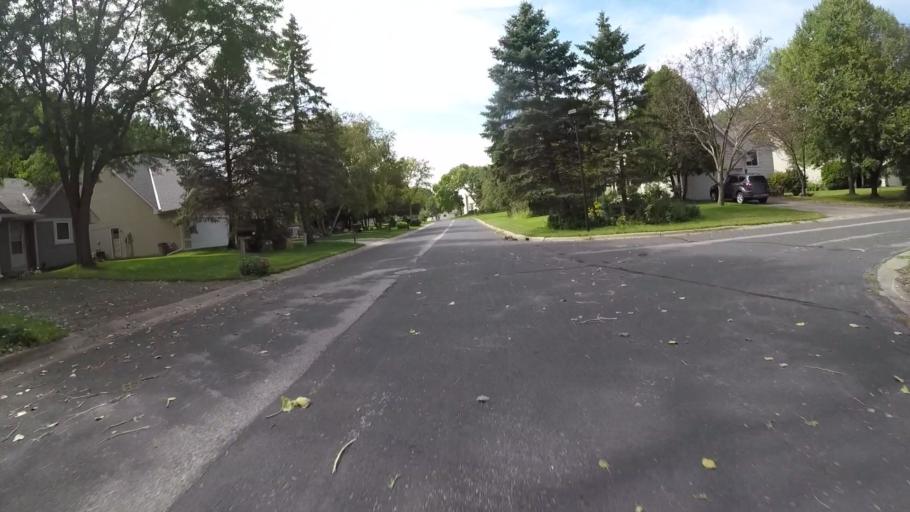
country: US
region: Minnesota
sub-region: Hennepin County
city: Eden Prairie
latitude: 44.8716
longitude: -93.4468
